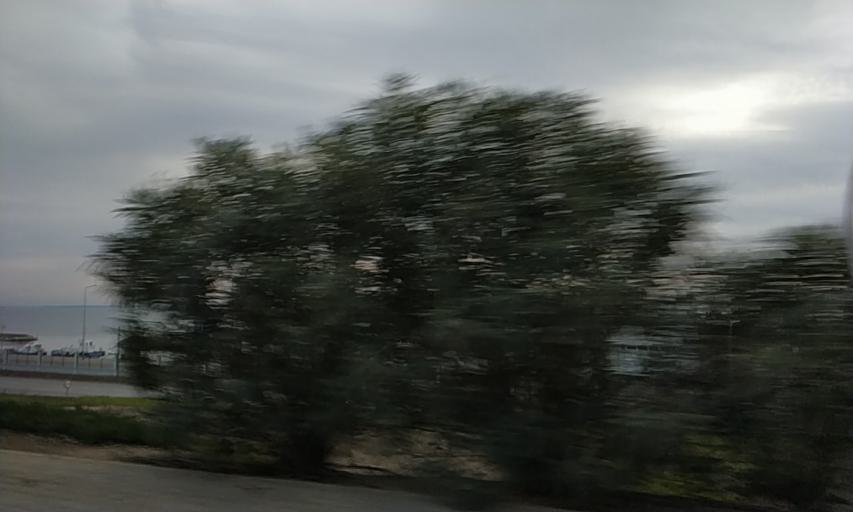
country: PT
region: Setubal
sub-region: Setubal
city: Setubal
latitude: 38.4967
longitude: -8.8347
